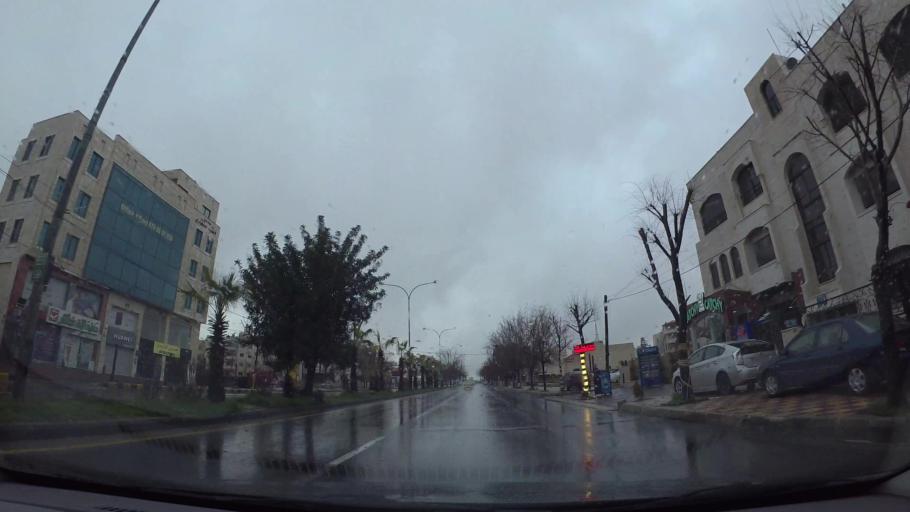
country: JO
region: Amman
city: Wadi as Sir
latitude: 31.9718
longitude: 35.8543
